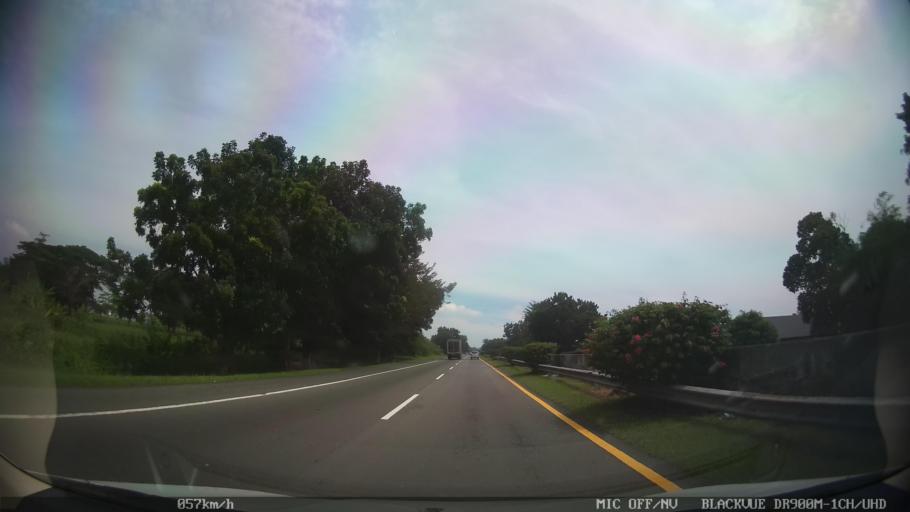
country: ID
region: North Sumatra
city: Labuhan Deli
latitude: 3.6930
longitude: 98.6820
